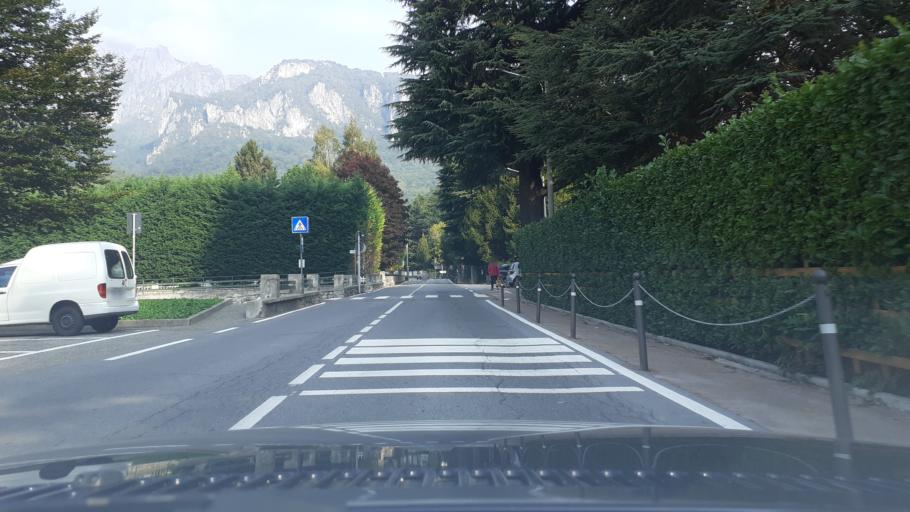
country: IT
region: Lombardy
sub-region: Provincia di Lecco
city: Ballabio
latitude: 45.8981
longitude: 9.4237
